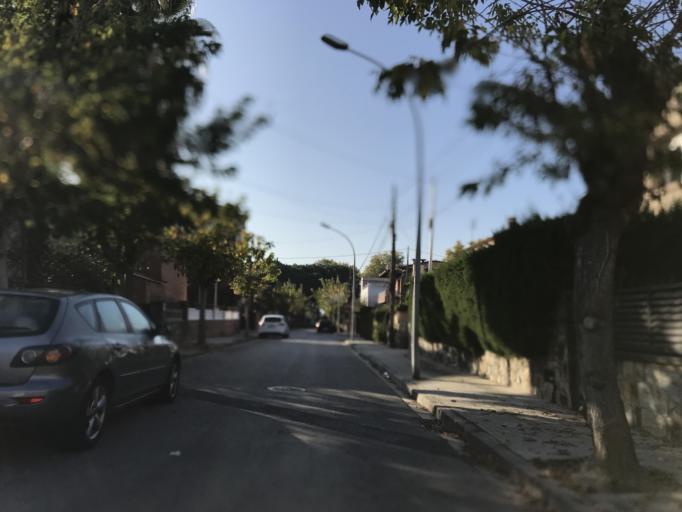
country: ES
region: Catalonia
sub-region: Provincia de Barcelona
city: Mollet del Valles
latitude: 41.5574
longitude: 2.2198
